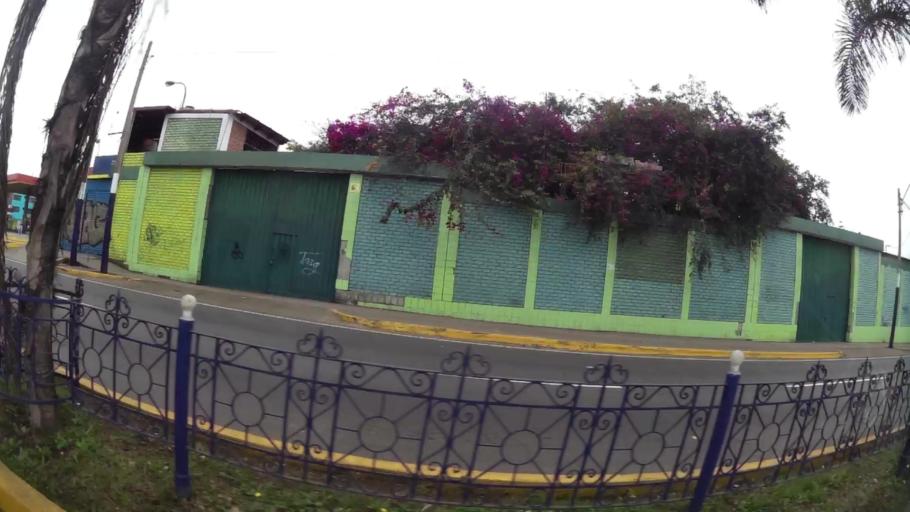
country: PE
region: Lima
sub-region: Lima
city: Surco
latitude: -12.1910
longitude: -77.0068
